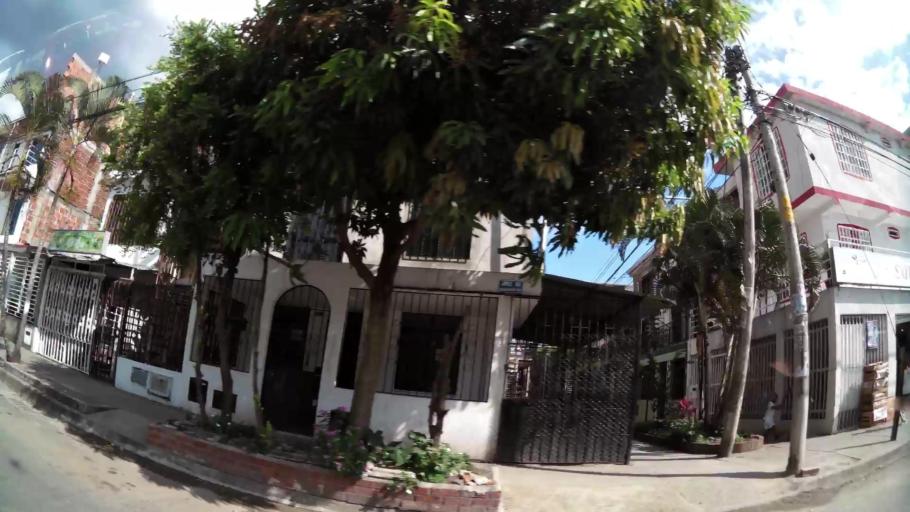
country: CO
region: Valle del Cauca
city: Cali
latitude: 3.3982
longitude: -76.5058
